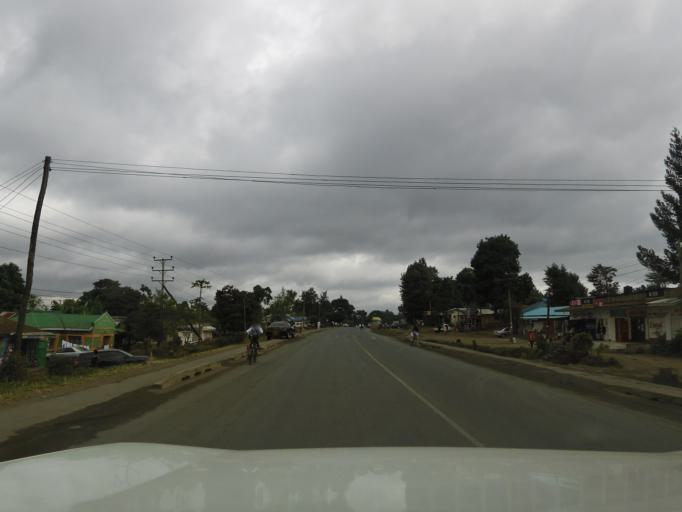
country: TZ
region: Arusha
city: Arusha
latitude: -3.3674
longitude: 36.7143
